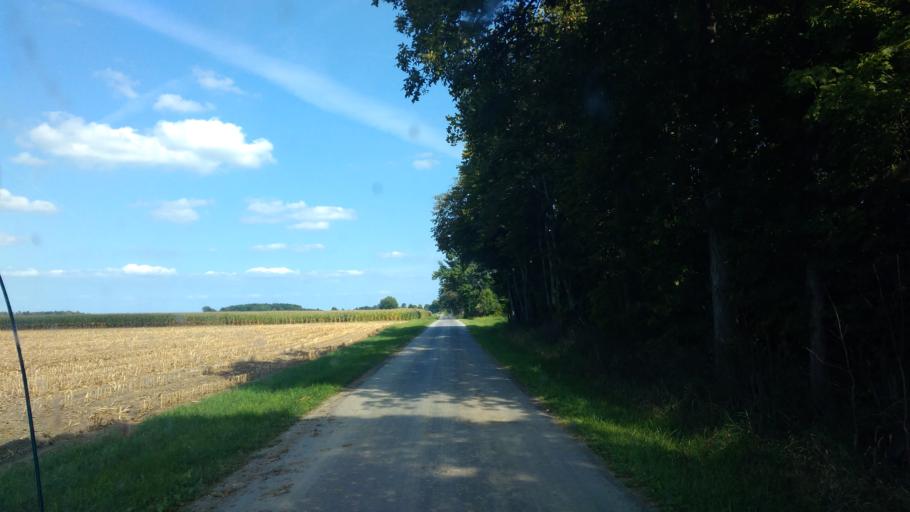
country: US
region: Ohio
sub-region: Hardin County
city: Kenton
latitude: 40.6284
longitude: -83.4832
